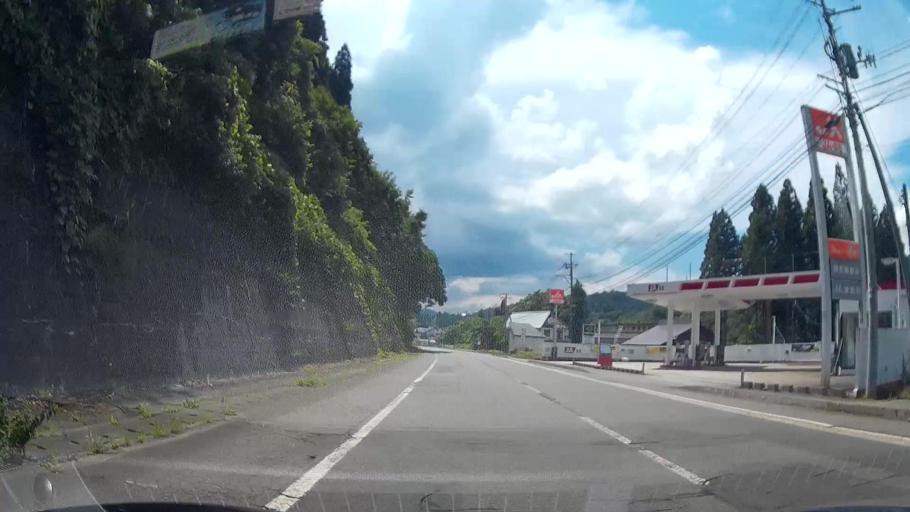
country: JP
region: Niigata
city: Tokamachi
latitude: 36.9941
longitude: 138.5941
